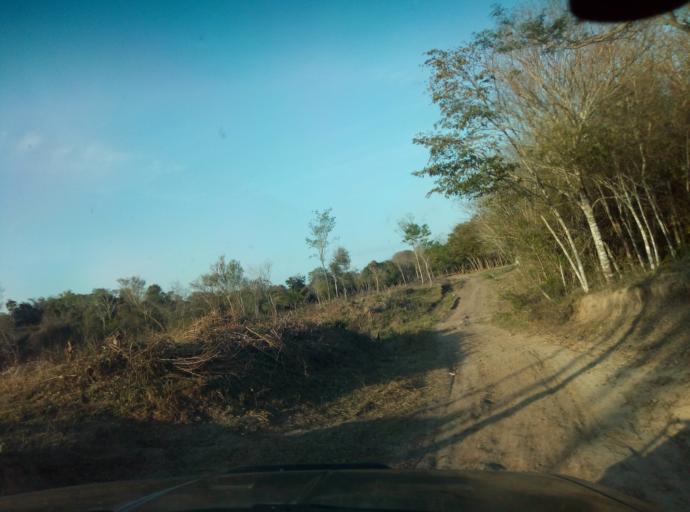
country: PY
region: Caaguazu
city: Yhu
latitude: -25.1987
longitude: -56.1123
